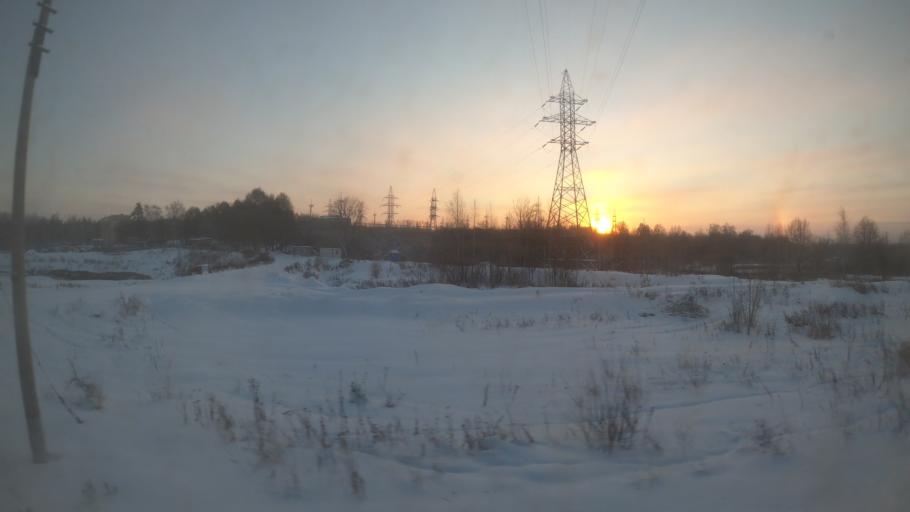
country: RU
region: Moskovskaya
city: Iksha
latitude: 56.1619
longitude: 37.5015
